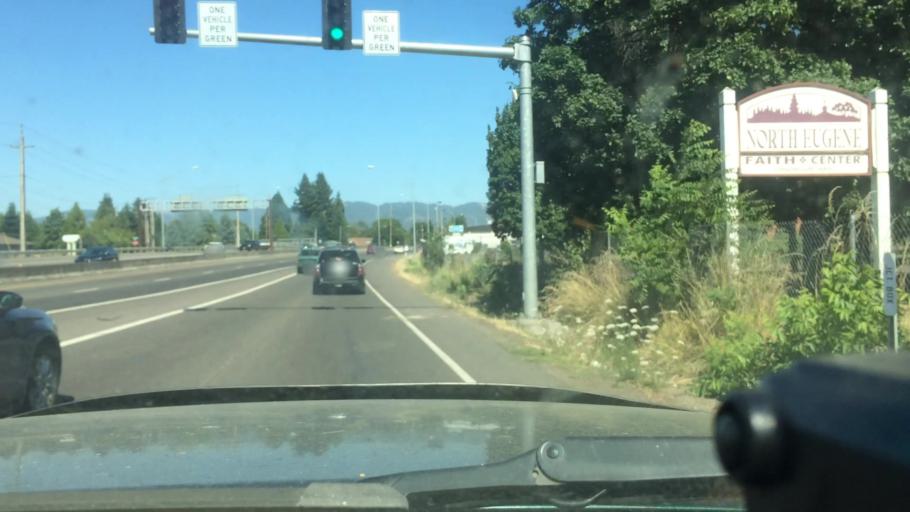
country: US
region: Oregon
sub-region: Lane County
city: Eugene
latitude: 44.0972
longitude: -123.1248
